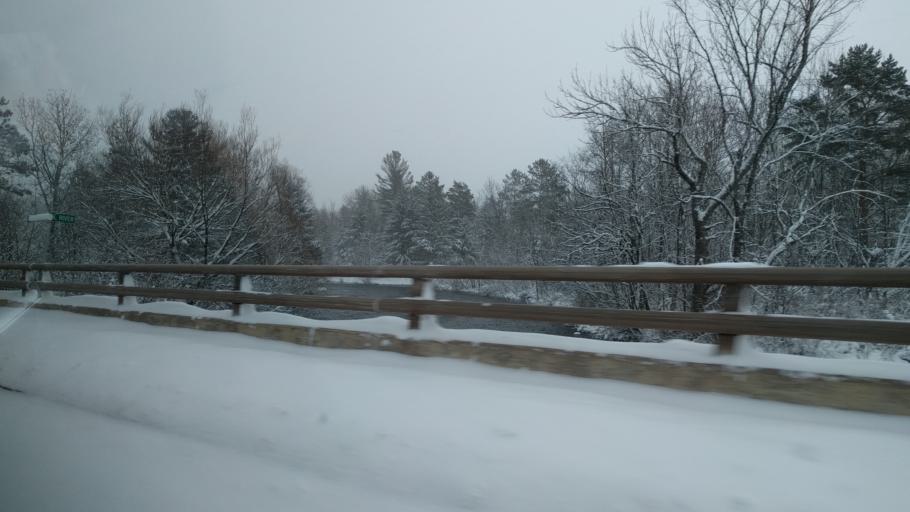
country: US
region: Wisconsin
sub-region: Iron County
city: Hurley
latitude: 46.4315
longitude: -90.2301
